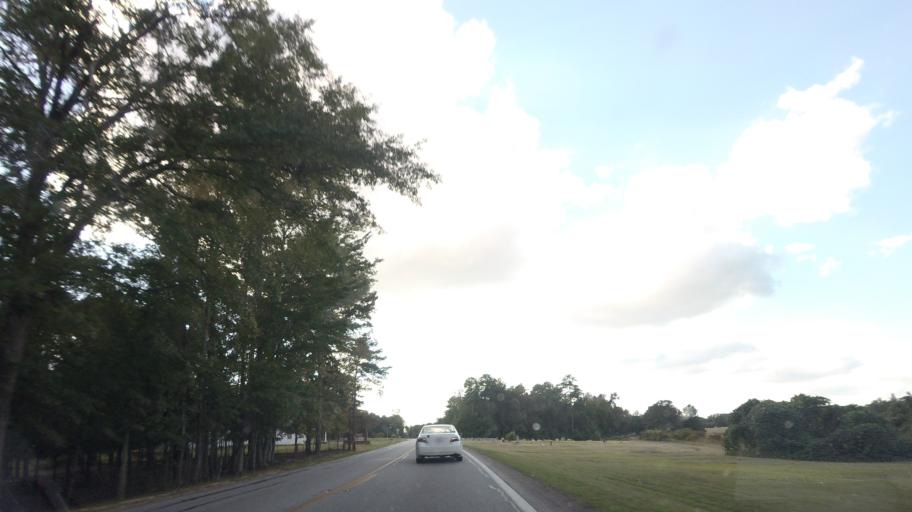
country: US
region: Georgia
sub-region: Lamar County
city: Barnesville
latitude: 33.0558
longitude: -84.0543
